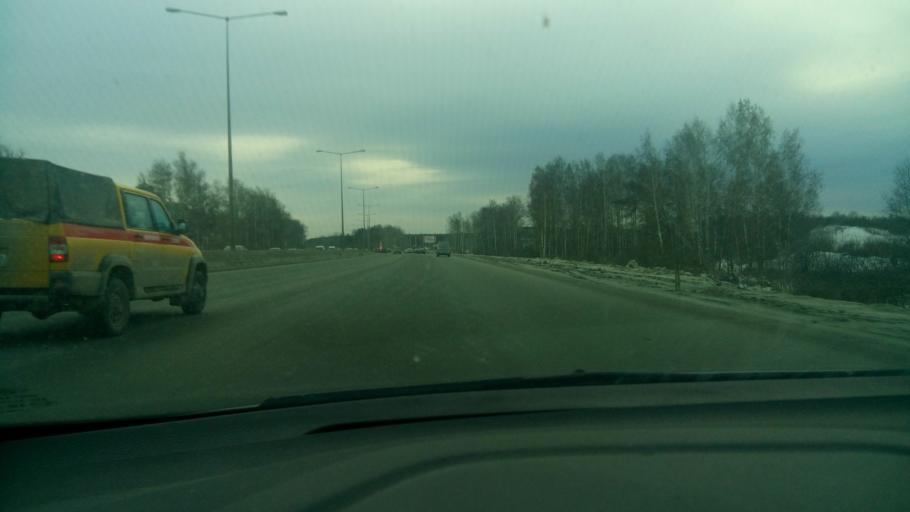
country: RU
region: Sverdlovsk
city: Istok
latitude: 56.7769
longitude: 60.7123
